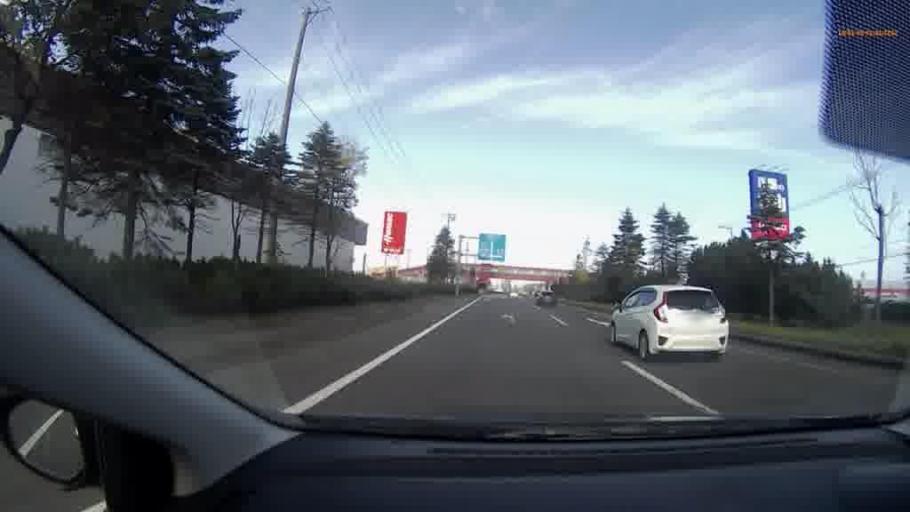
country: JP
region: Hokkaido
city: Kushiro
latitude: 43.0098
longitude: 144.4110
